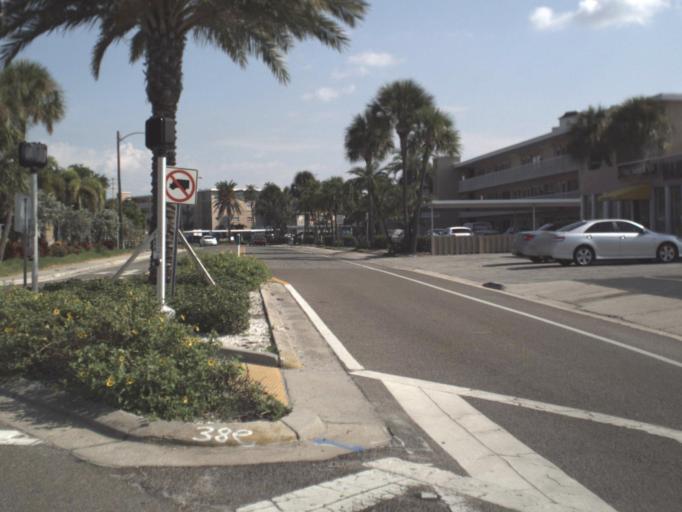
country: US
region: Florida
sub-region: Pinellas County
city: Saint Pete Beach
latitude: 27.7329
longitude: -82.7452
